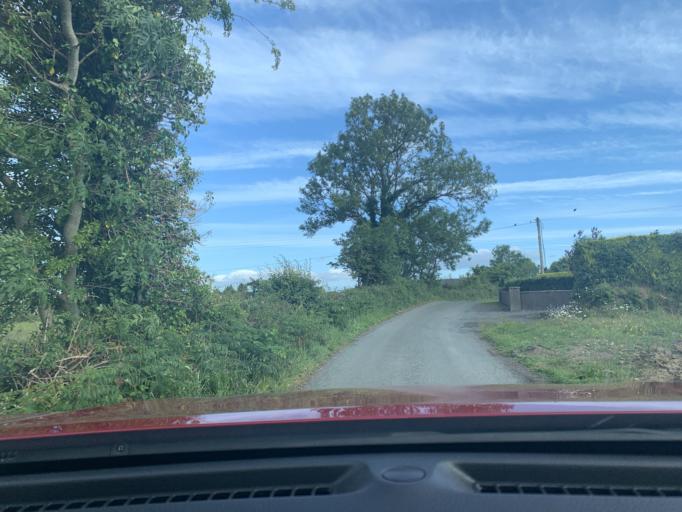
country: IE
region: Connaught
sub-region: Sligo
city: Sligo
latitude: 54.2362
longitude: -8.4696
